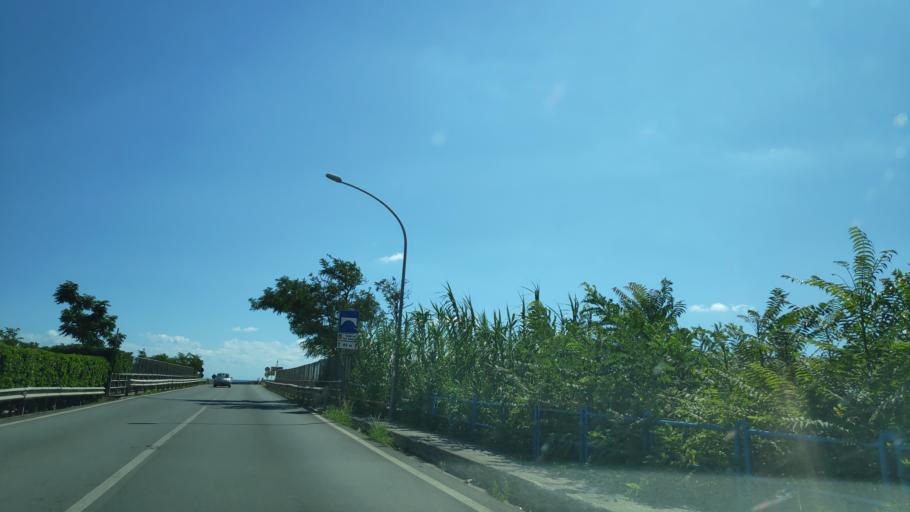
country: IT
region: Calabria
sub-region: Provincia di Cosenza
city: Campora San Giovanni
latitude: 39.0667
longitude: 16.0920
